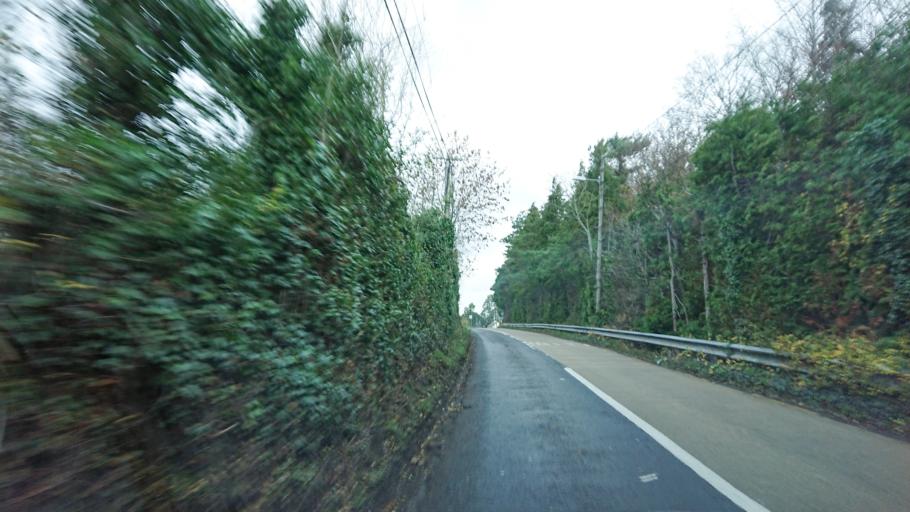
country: IE
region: Munster
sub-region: South Tipperary
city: Cluain Meala
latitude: 52.3528
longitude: -7.6754
